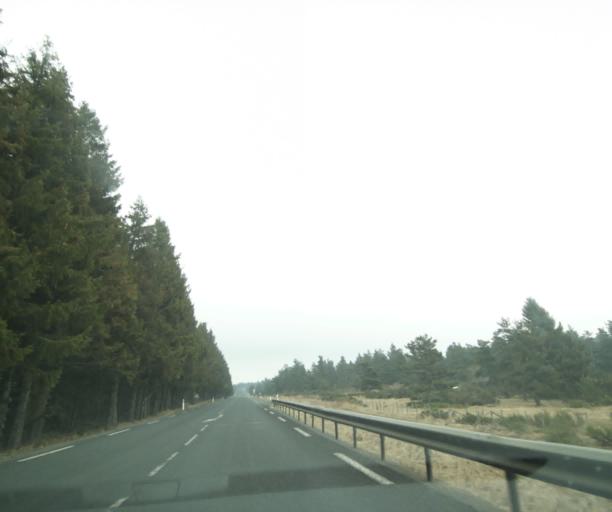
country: FR
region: Languedoc-Roussillon
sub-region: Departement de la Lozere
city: Langogne
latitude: 44.7515
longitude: 3.9537
